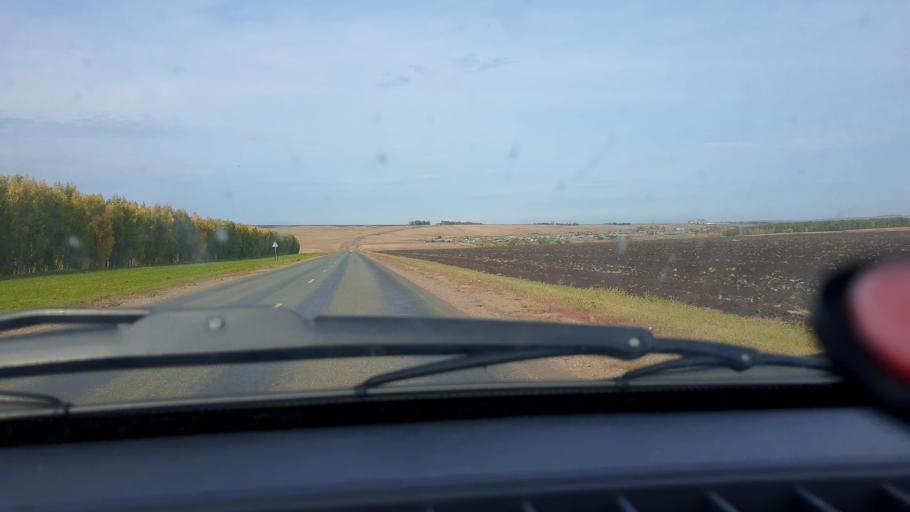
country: RU
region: Bashkortostan
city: Chekmagush
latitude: 54.9823
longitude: 54.5764
